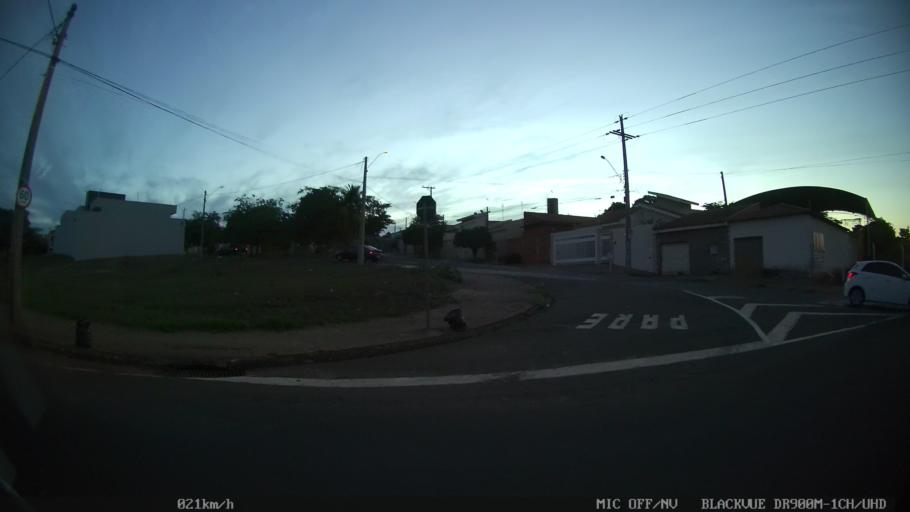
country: BR
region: Sao Paulo
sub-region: Catanduva
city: Catanduva
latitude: -21.1417
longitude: -48.9902
